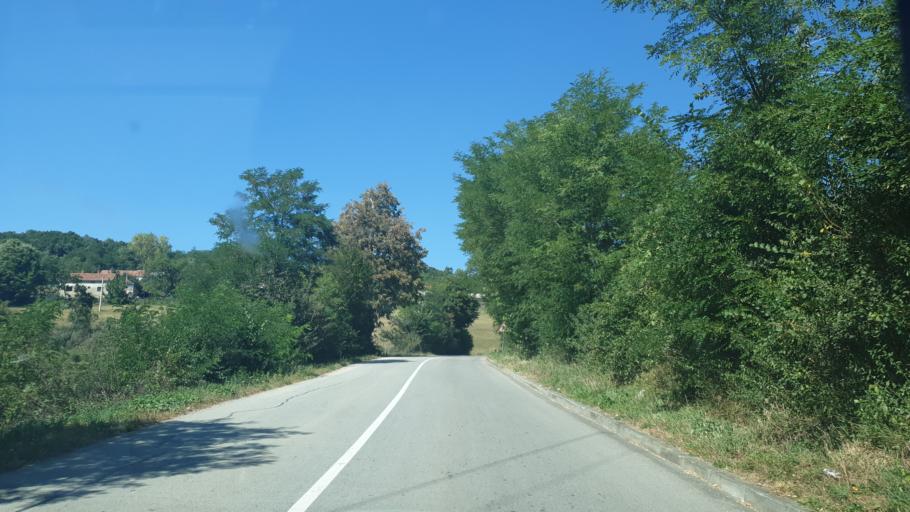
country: RS
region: Central Serbia
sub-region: Kolubarski Okrug
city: Mionica
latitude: 44.1966
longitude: 20.0246
